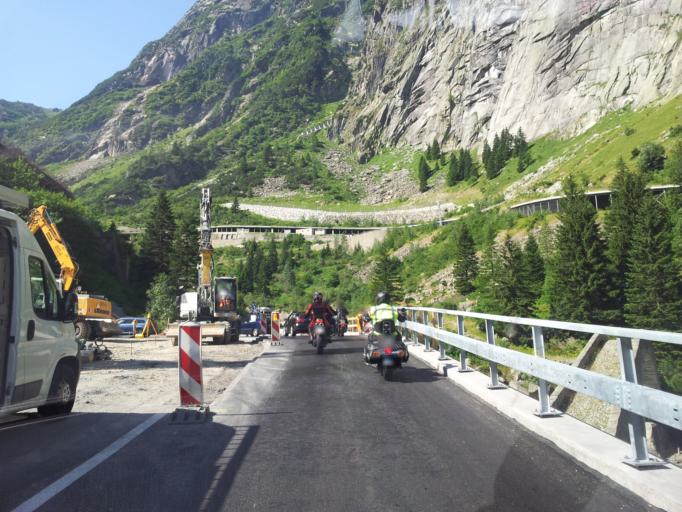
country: CH
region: Uri
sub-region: Uri
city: Andermatt
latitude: 46.6587
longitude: 8.5850
